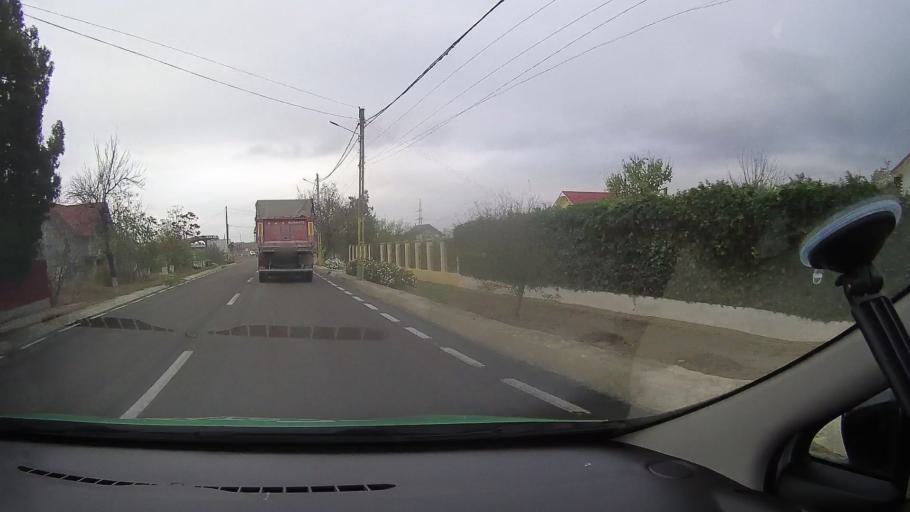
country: RO
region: Constanta
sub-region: Comuna Poarta Alba
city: Poarta Alba
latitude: 44.2107
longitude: 28.3946
